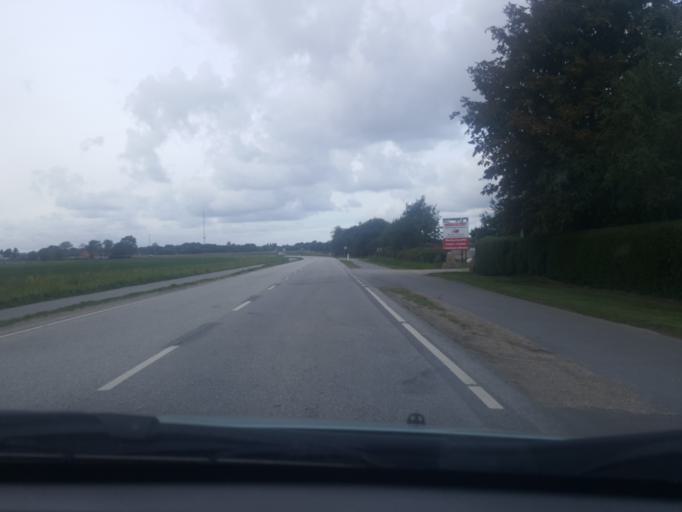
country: DK
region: Zealand
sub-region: Guldborgsund Kommune
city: Nykobing Falster
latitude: 54.6987
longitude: 11.9474
